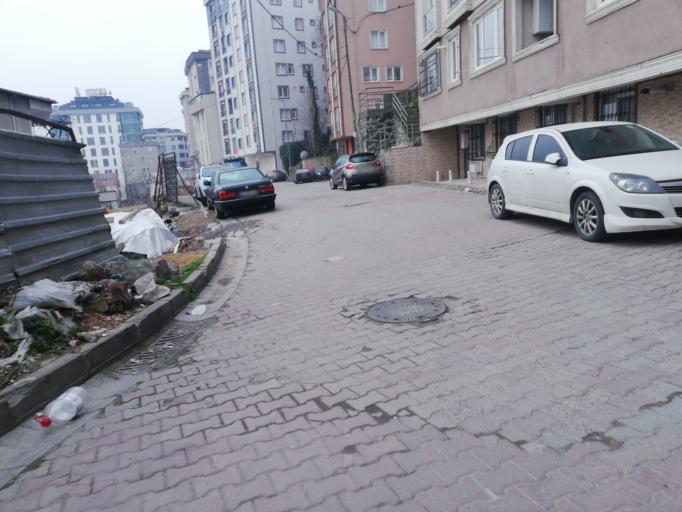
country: TR
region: Istanbul
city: Sisli
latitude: 41.0858
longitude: 28.9720
